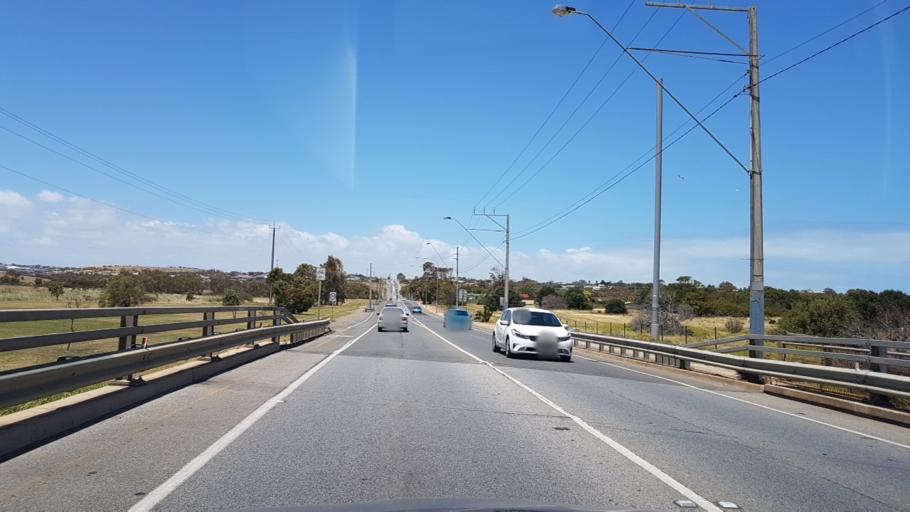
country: AU
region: South Australia
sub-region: Onkaparinga
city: Moana
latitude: -35.2034
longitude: 138.4785
